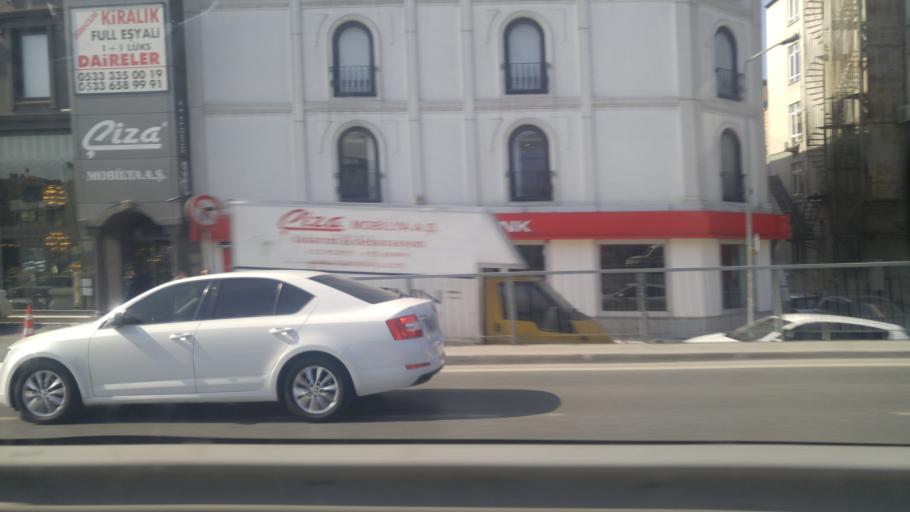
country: TR
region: Istanbul
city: Bahcelievler
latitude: 40.9940
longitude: 28.7946
